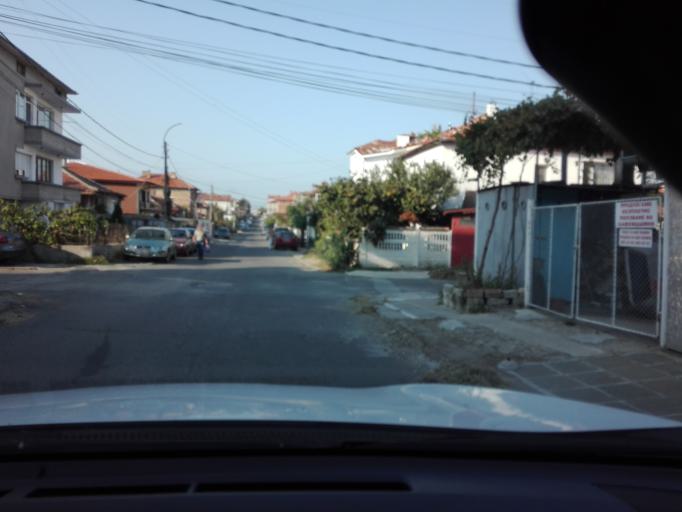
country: BG
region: Burgas
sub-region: Obshtina Burgas
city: Burgas
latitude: 42.4593
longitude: 27.4089
